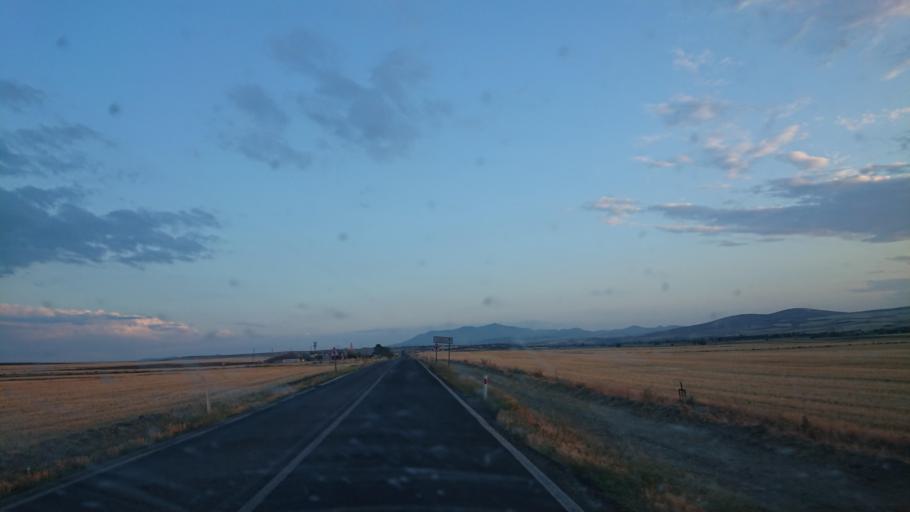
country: TR
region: Aksaray
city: Balci
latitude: 38.8266
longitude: 34.1374
